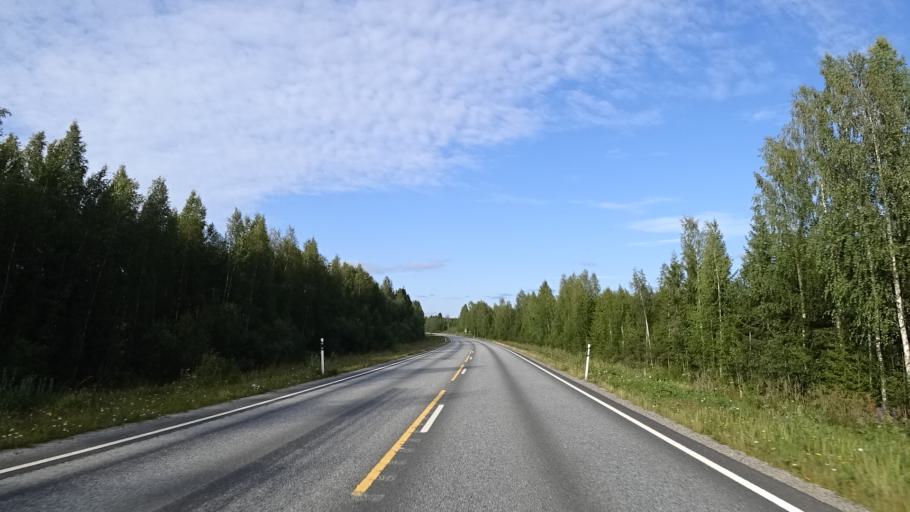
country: FI
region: North Karelia
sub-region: Joensuu
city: Eno
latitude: 62.8159
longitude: 30.1821
